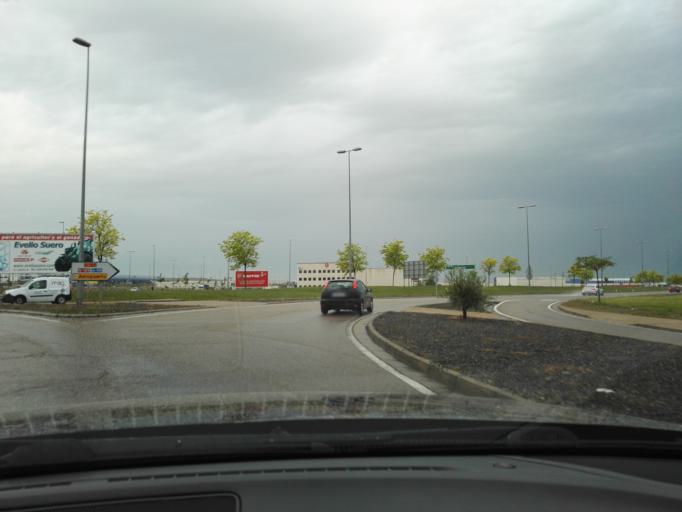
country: ES
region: Aragon
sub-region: Provincia de Zaragoza
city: Montecanal
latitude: 41.6400
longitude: -0.9922
